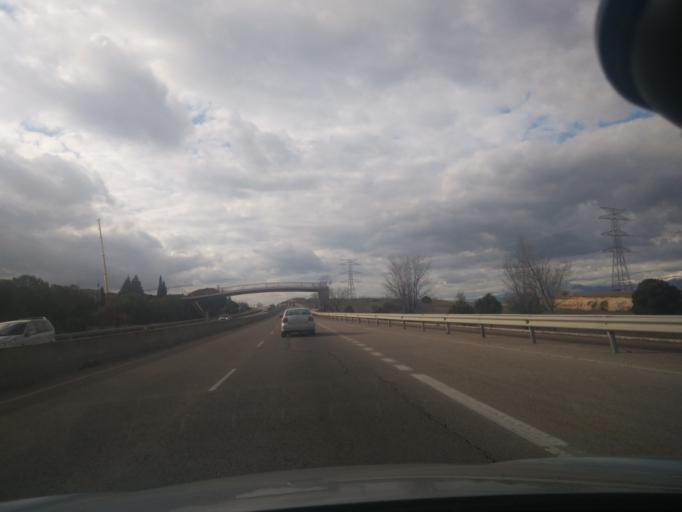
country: ES
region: Madrid
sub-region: Provincia de Madrid
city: Alcobendas
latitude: 40.5524
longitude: -3.6729
